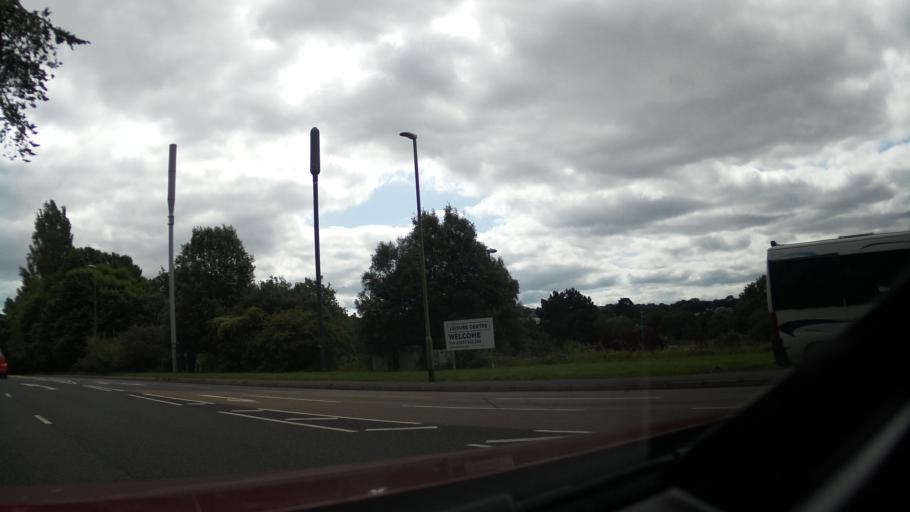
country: GB
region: England
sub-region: Borough of Torbay
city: Paignton
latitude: 50.4249
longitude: -3.5632
